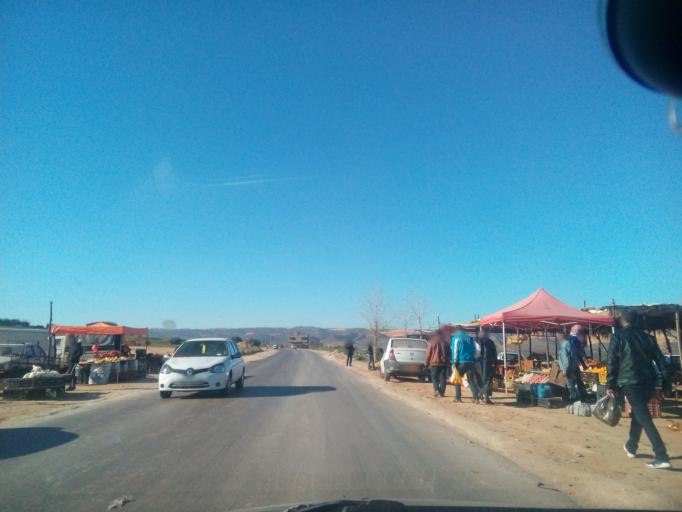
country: DZ
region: Relizane
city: Relizane
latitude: 35.9121
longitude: 0.5032
